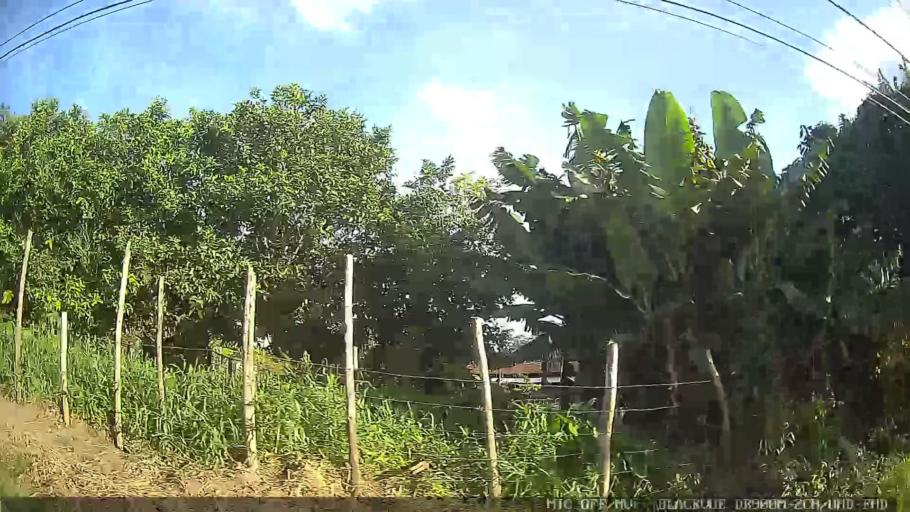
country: BR
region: Sao Paulo
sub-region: Mogi das Cruzes
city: Mogi das Cruzes
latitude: -23.5091
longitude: -46.1215
